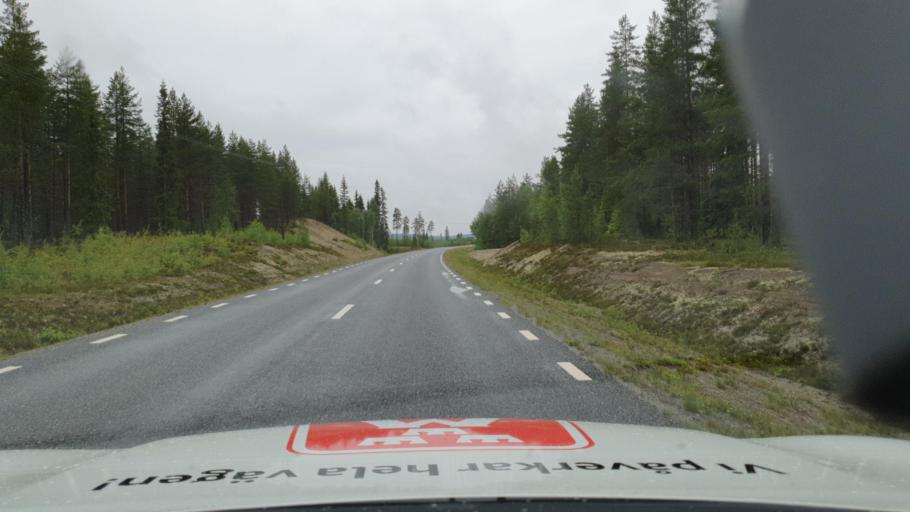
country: SE
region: Vaesterbotten
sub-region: Asele Kommun
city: Asele
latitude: 63.9495
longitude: 17.2746
